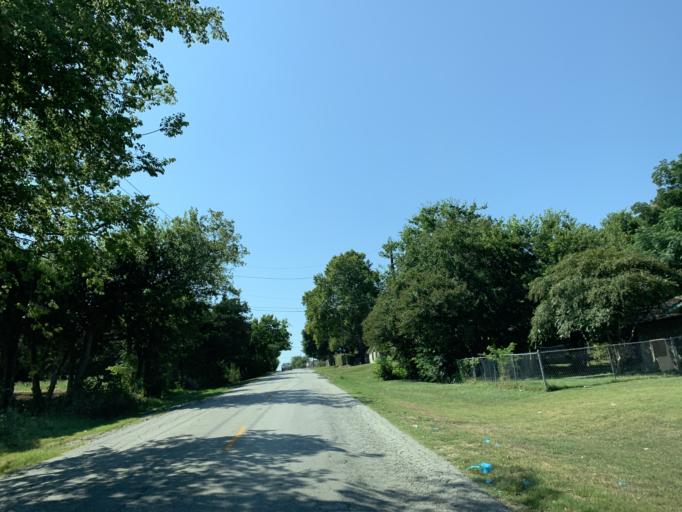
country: US
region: Texas
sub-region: Dallas County
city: Hutchins
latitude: 32.6718
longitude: -96.7460
